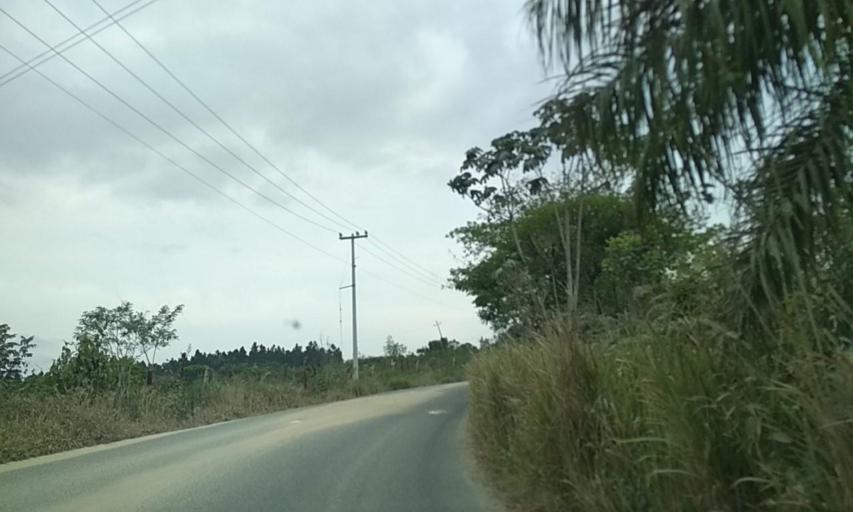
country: MX
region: Veracruz
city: Las Choapas
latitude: 17.8001
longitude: -94.1107
